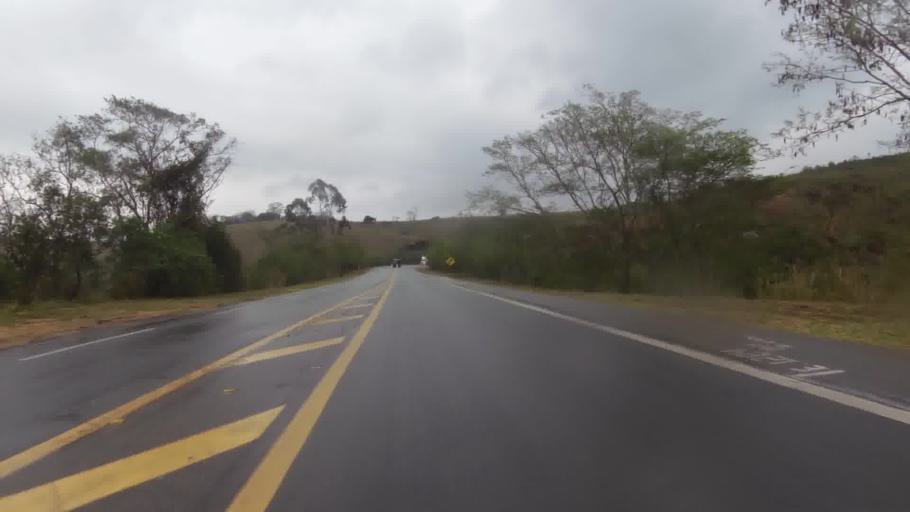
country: BR
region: Espirito Santo
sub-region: Rio Novo Do Sul
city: Rio Novo do Sul
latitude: -20.8990
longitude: -41.0210
